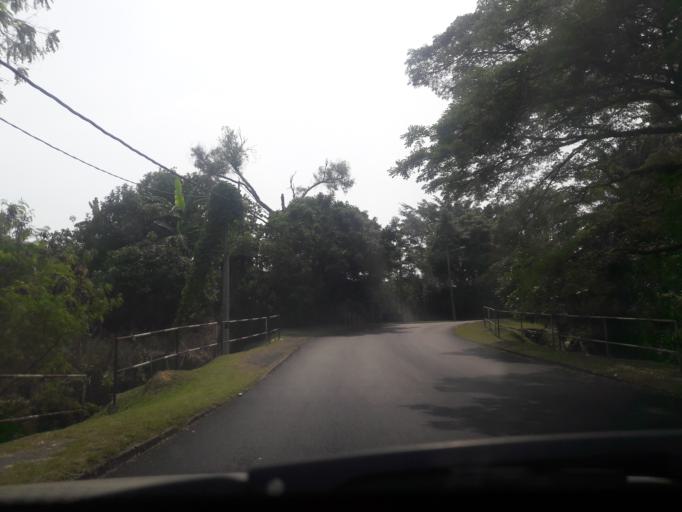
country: MY
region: Kedah
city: Kulim
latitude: 5.3694
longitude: 100.5631
